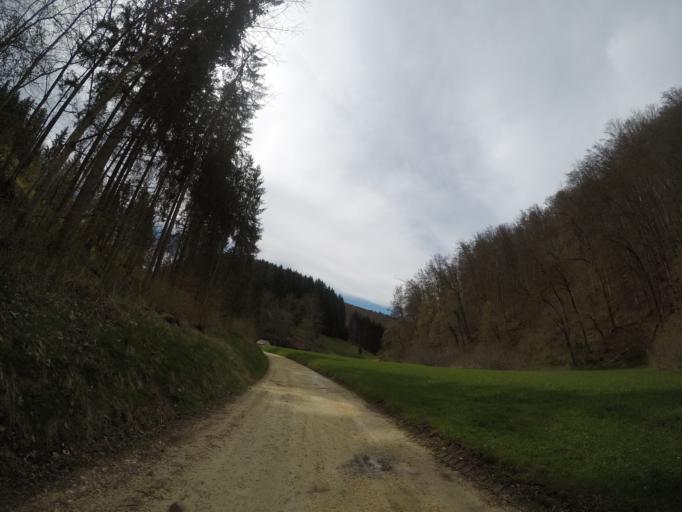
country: DE
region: Baden-Wuerttemberg
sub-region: Regierungsbezirk Stuttgart
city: Wiesensteig
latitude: 48.5506
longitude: 9.6023
